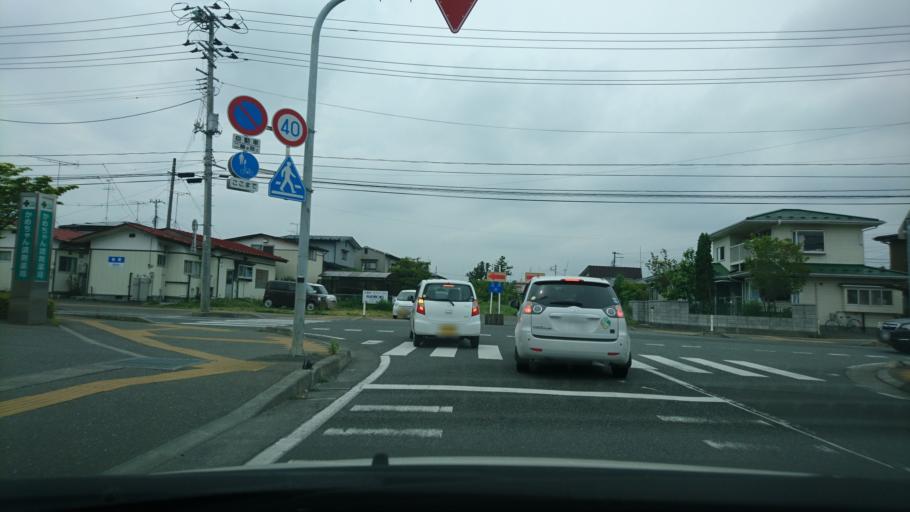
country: JP
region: Iwate
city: Ichinoseki
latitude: 38.9352
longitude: 141.1136
